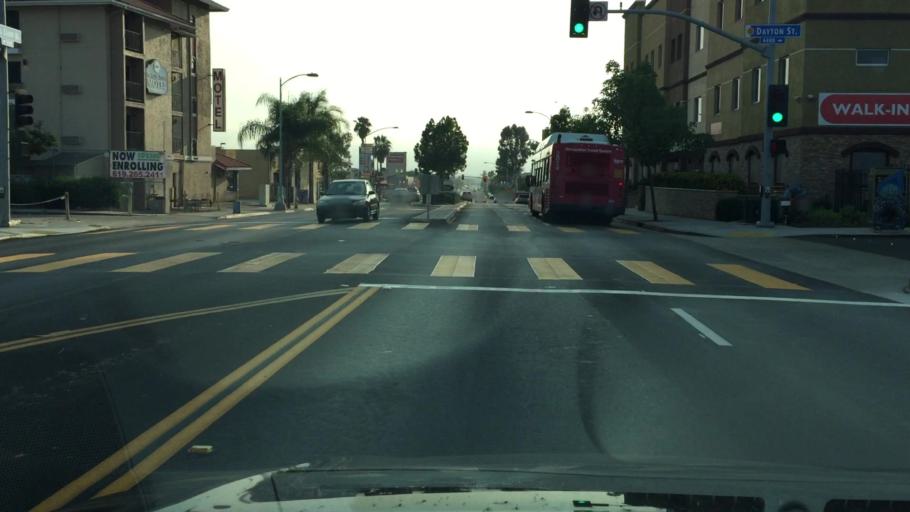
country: US
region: California
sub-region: San Diego County
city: Lemon Grove
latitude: 32.7582
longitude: -117.0773
